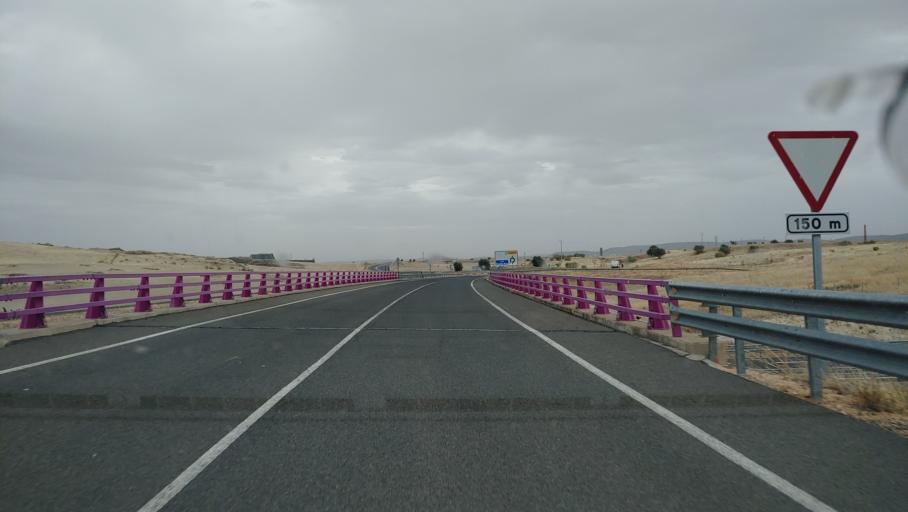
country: ES
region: Castille-La Mancha
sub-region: Provincia de Ciudad Real
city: Canada de Calatrava
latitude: 38.8749
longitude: -4.0099
